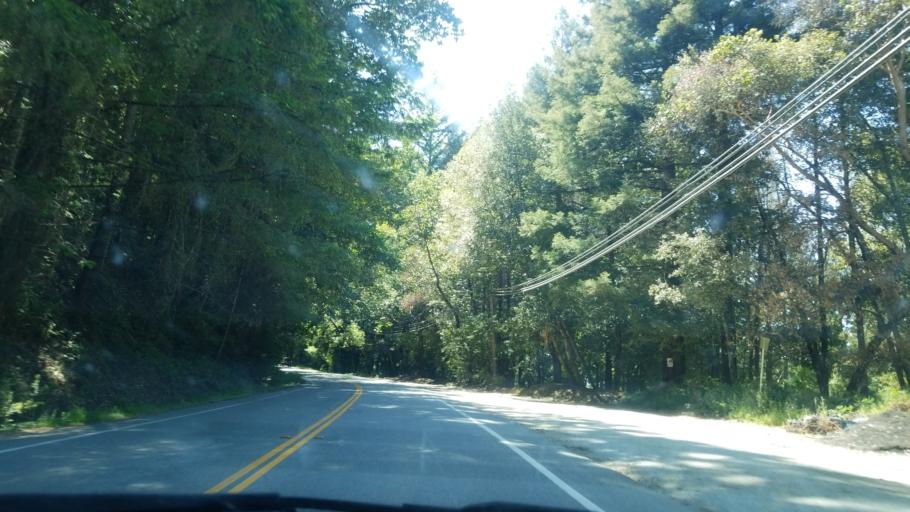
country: US
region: California
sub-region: Santa Clara County
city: Lexington Hills
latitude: 37.1183
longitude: -121.9281
